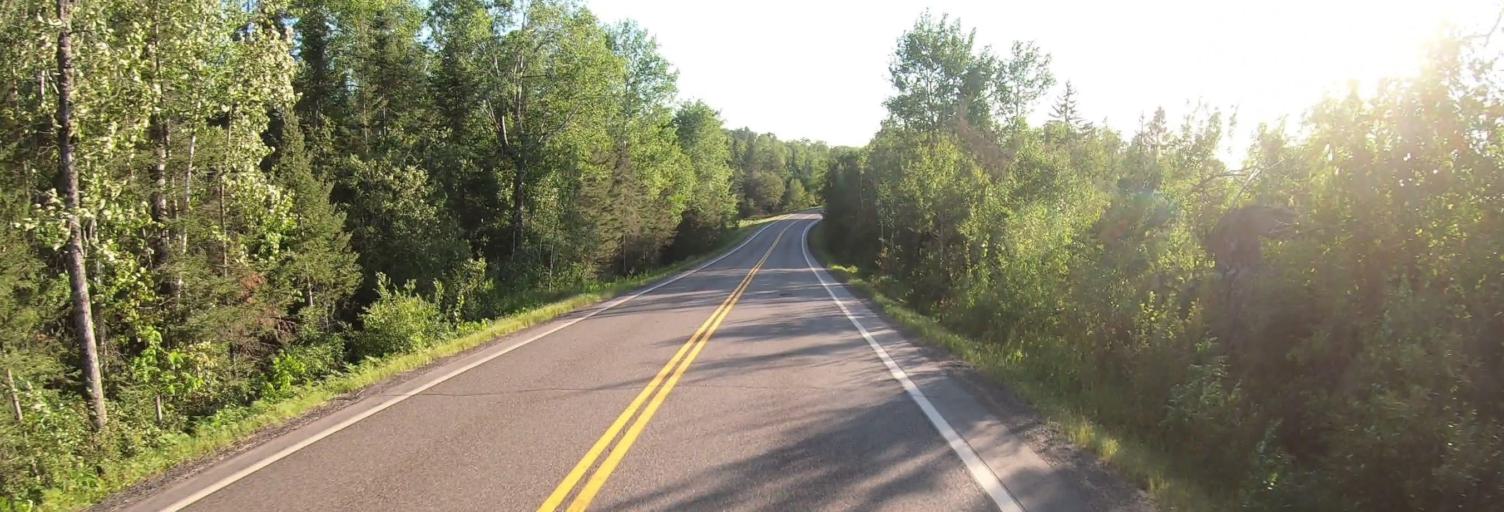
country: US
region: Minnesota
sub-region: Saint Louis County
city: Ely
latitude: 47.9592
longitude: -91.5900
